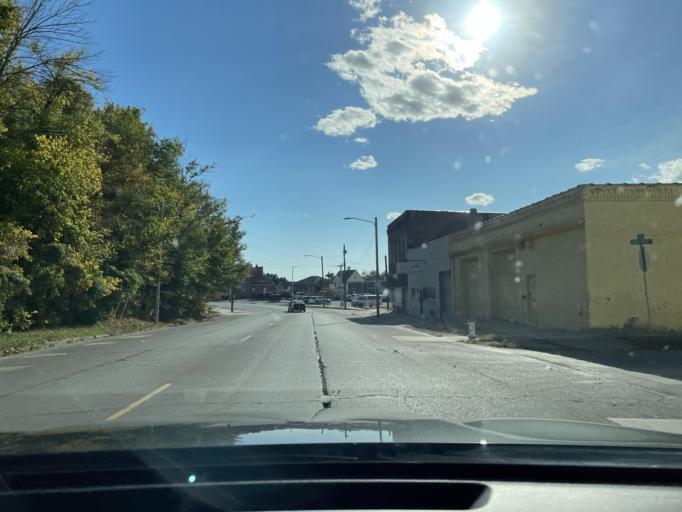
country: US
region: Kansas
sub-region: Doniphan County
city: Elwood
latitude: 39.7200
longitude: -94.8618
